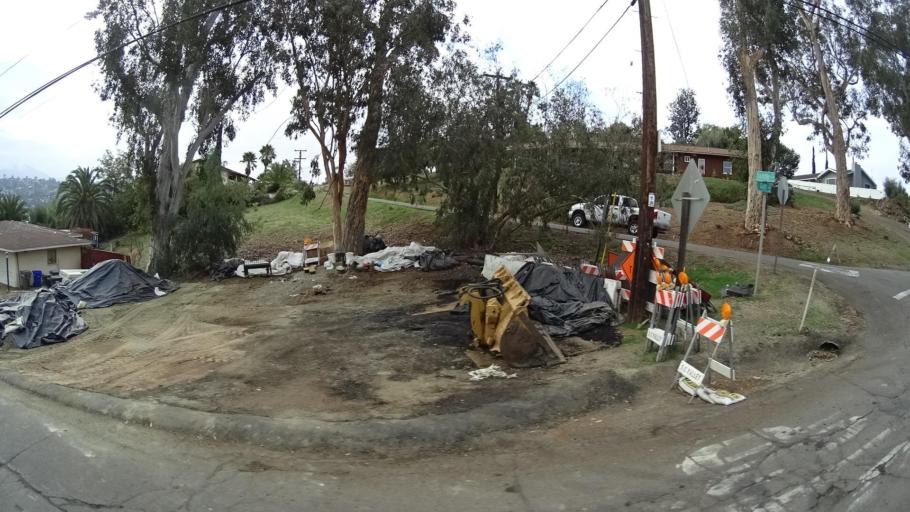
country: US
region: California
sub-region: San Diego County
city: Spring Valley
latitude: 32.7474
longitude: -117.0083
